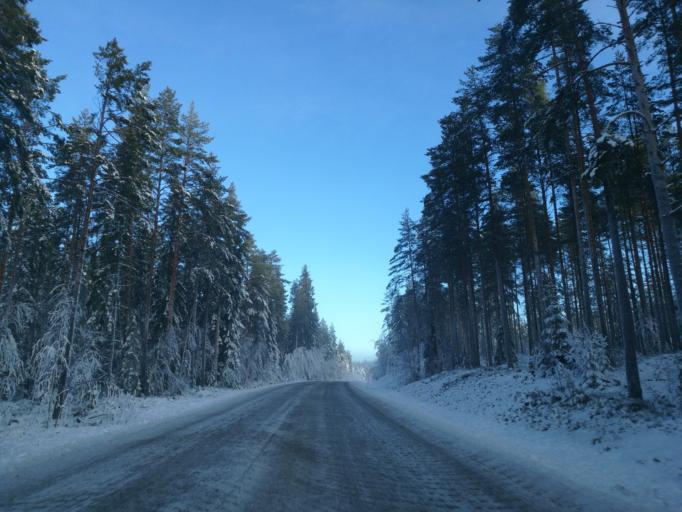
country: NO
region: Hedmark
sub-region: Grue
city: Kirkenaer
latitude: 60.3849
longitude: 12.3598
